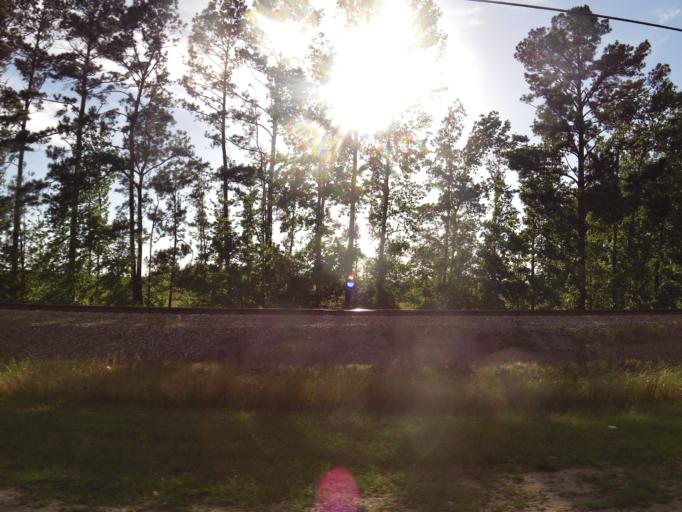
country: US
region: South Carolina
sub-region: Hampton County
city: Estill
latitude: 32.7399
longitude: -81.2417
